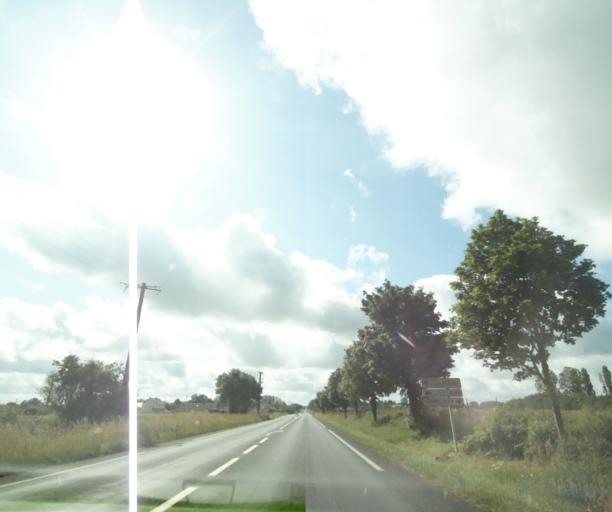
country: FR
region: Pays de la Loire
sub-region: Departement de la Sarthe
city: Solesmes
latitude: 47.8111
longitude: -0.2823
